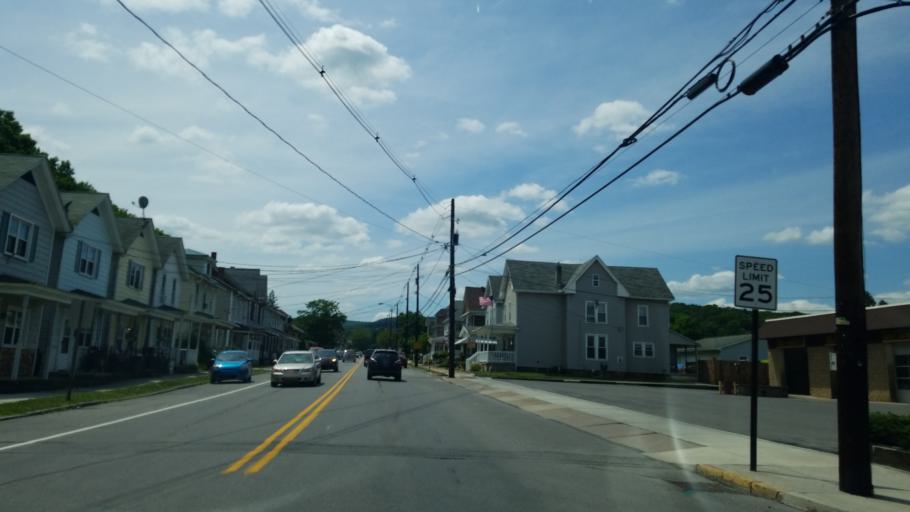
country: US
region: Pennsylvania
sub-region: Blair County
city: Tyrone
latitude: 40.6781
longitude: -78.2406
